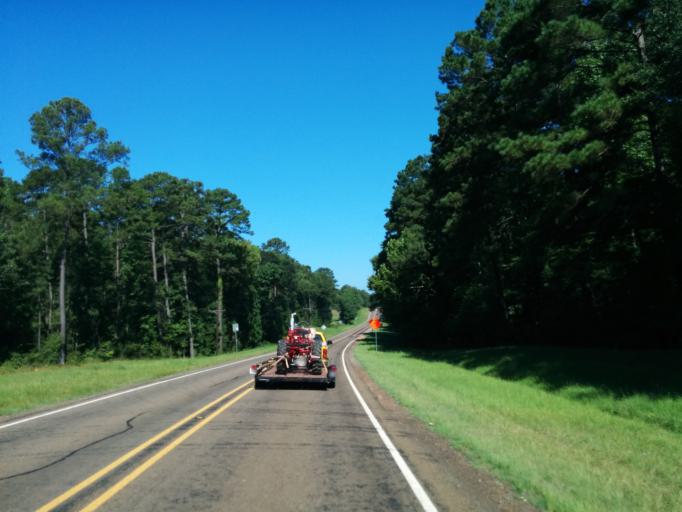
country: US
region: Texas
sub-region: Sabine County
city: Milam
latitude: 31.4293
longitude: -93.8104
